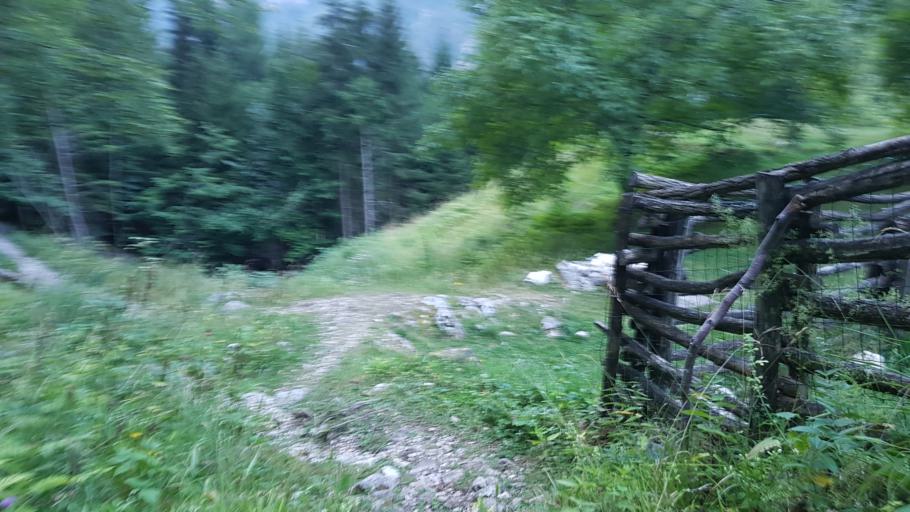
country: SI
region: Kranjska Gora
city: Kranjska Gora
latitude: 46.3681
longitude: 13.7480
